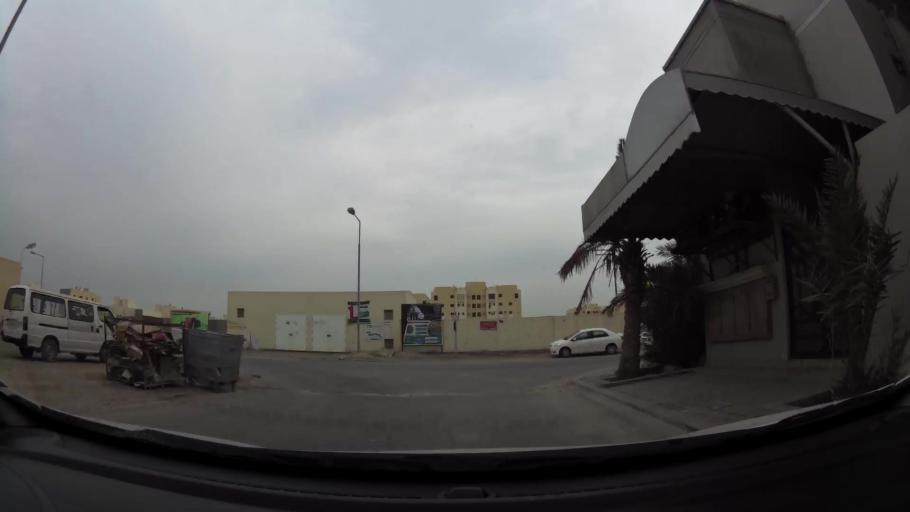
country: BH
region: Northern
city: Sitrah
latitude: 26.1404
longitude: 50.5968
